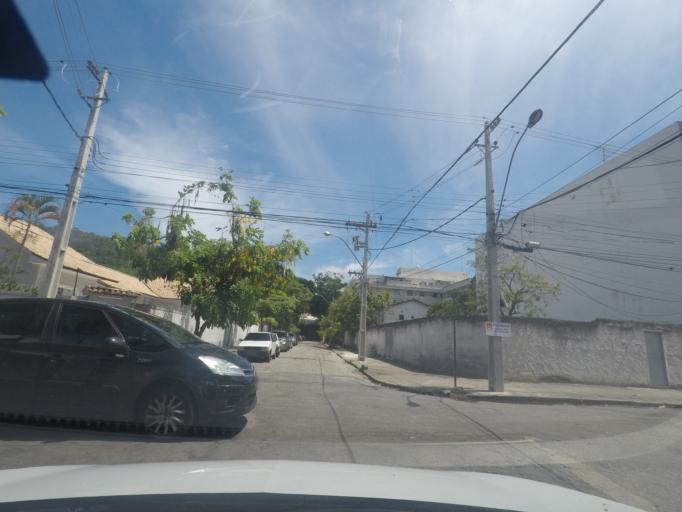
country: BR
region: Rio de Janeiro
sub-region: Niteroi
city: Niteroi
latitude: -22.9174
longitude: -43.0936
